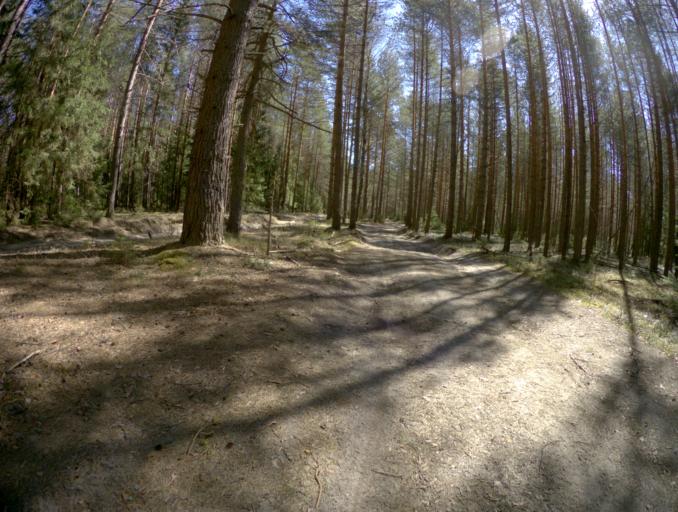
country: RU
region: Vladimir
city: Golovino
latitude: 55.9110
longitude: 40.4381
